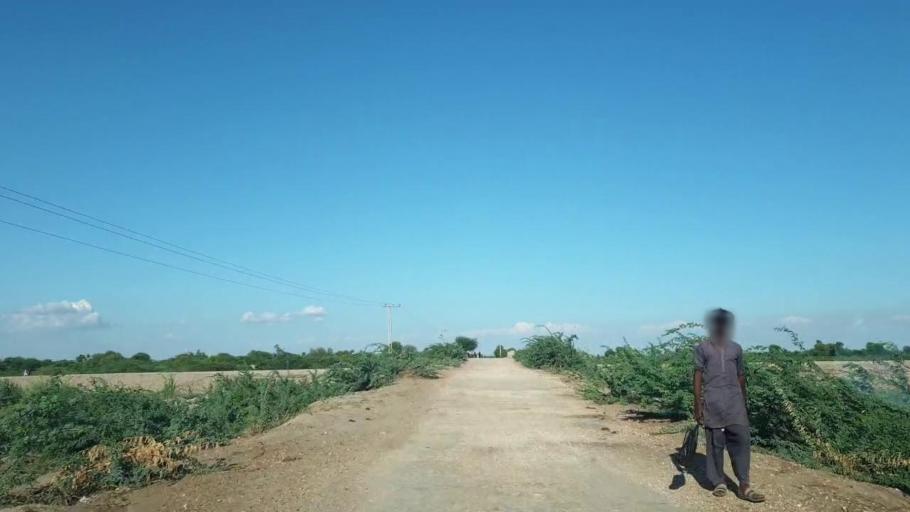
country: PK
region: Sindh
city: Dhoro Naro
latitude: 25.6396
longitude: 69.4892
